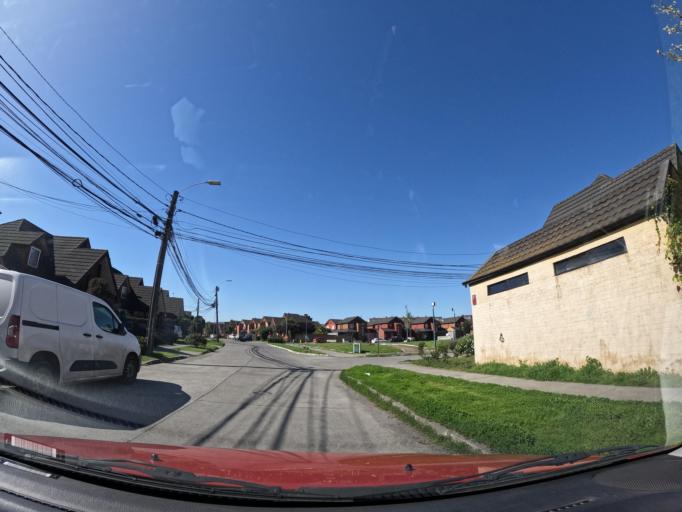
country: CL
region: Biobio
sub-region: Provincia de Concepcion
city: Concepcion
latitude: -36.8838
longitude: -73.1442
